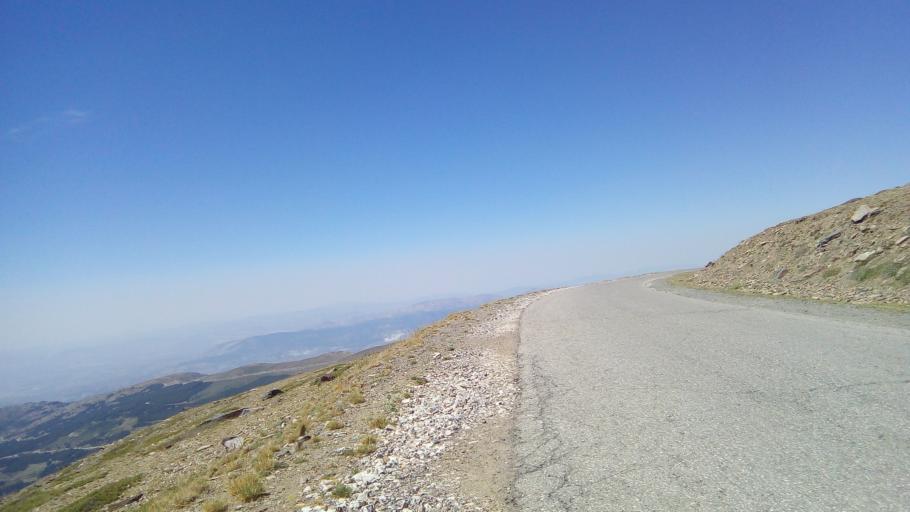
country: ES
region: Andalusia
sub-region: Provincia de Granada
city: Guejar-Sierra
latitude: 37.0792
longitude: -3.3835
